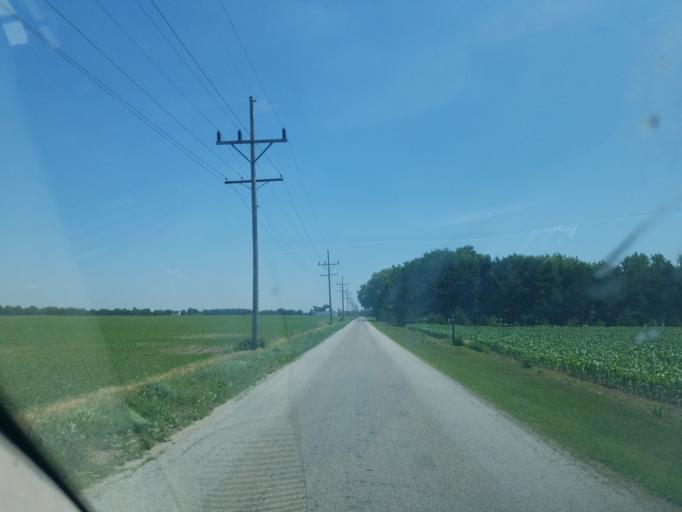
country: US
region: Ohio
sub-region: Allen County
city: Delphos
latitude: 40.7795
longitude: -84.3184
